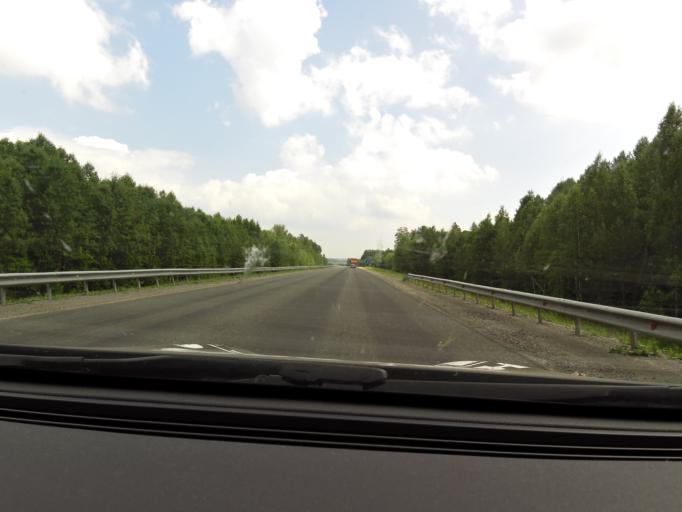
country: RU
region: Sverdlovsk
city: Achit
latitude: 56.7794
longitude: 57.9837
